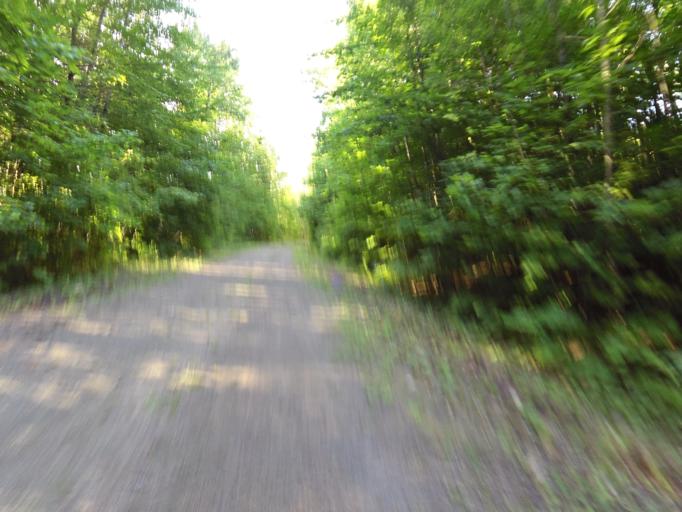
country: CA
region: Quebec
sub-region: Outaouais
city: Maniwaki
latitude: 46.2564
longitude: -76.0226
